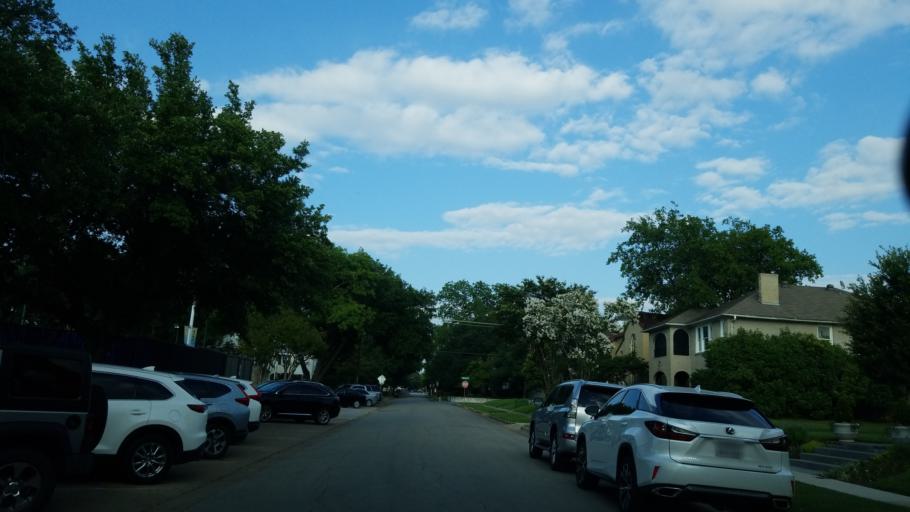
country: US
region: Texas
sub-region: Dallas County
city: University Park
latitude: 32.8503
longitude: -96.7911
